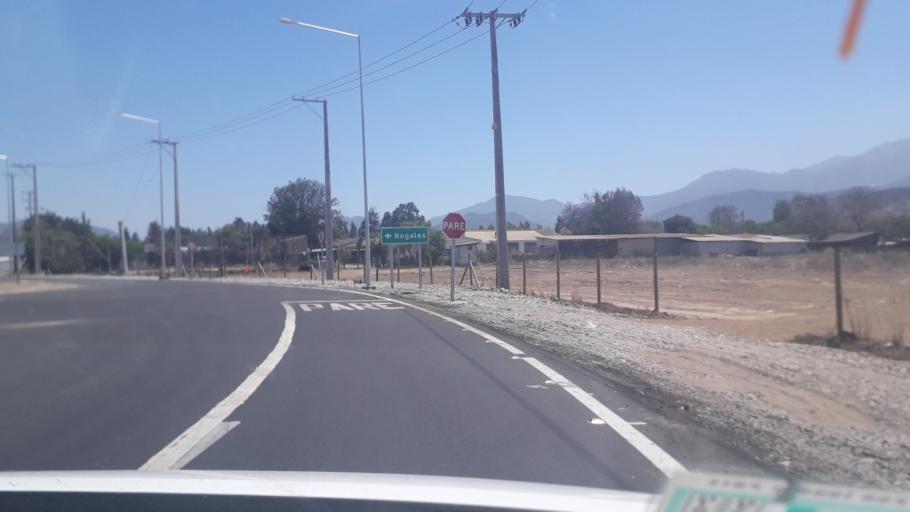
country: CL
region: Valparaiso
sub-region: Provincia de Quillota
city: Hacienda La Calera
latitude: -32.7374
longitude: -71.1985
